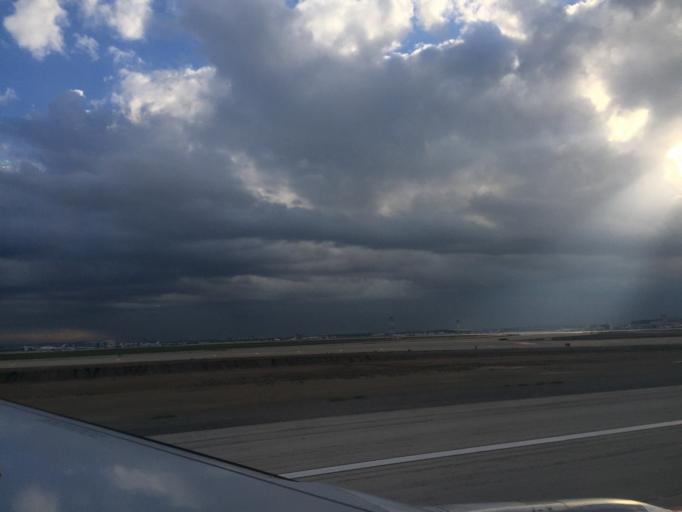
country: IL
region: Central District
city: Yehud
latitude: 32.0170
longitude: 34.8881
